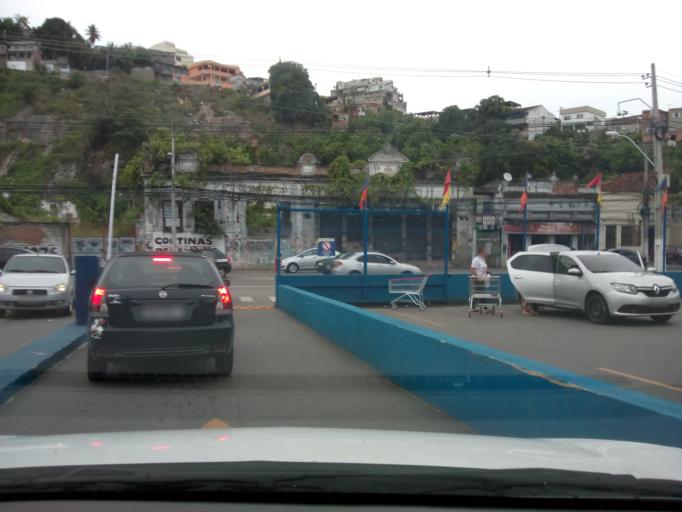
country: BR
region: Rio de Janeiro
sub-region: Niteroi
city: Niteroi
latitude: -22.8777
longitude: -43.1093
